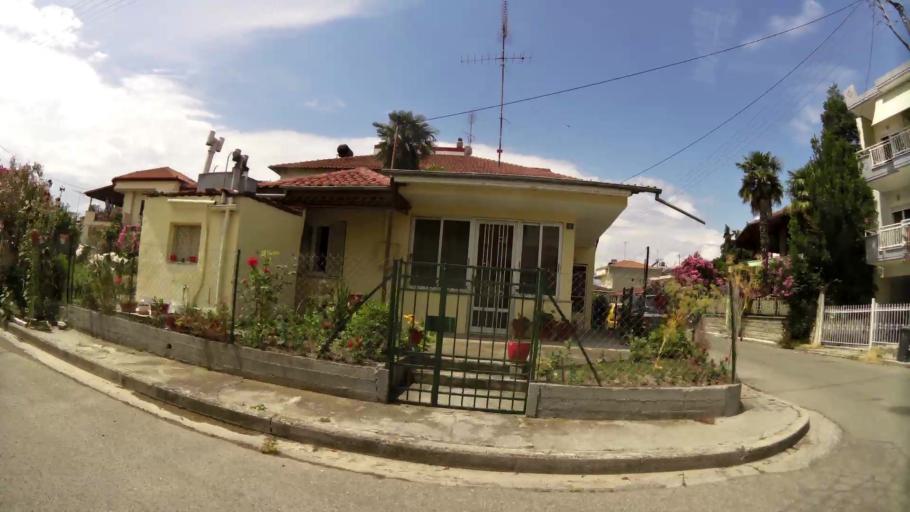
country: GR
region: Central Macedonia
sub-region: Nomos Pierias
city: Katerini
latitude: 40.2631
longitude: 22.5012
